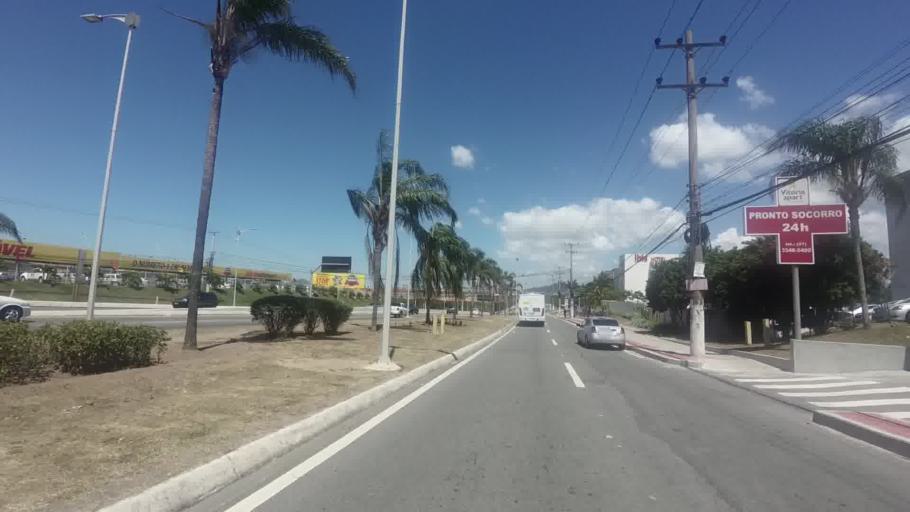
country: BR
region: Espirito Santo
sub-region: Vila Velha
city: Vila Velha
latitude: -20.2374
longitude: -40.2780
